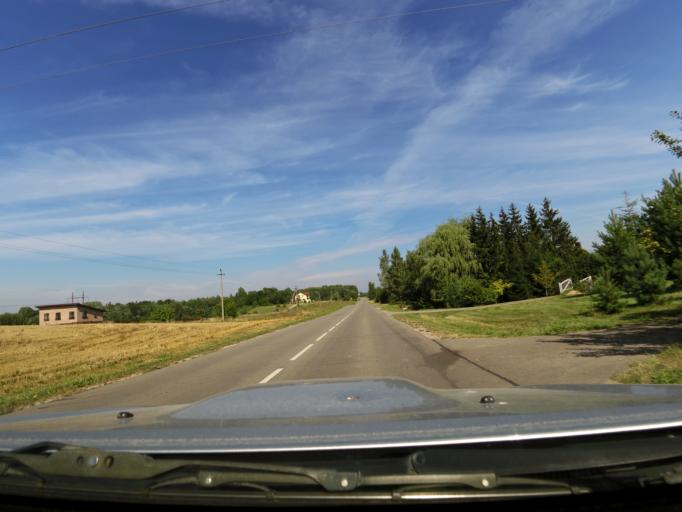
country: LT
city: Grigiskes
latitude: 54.7855
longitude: 25.0894
